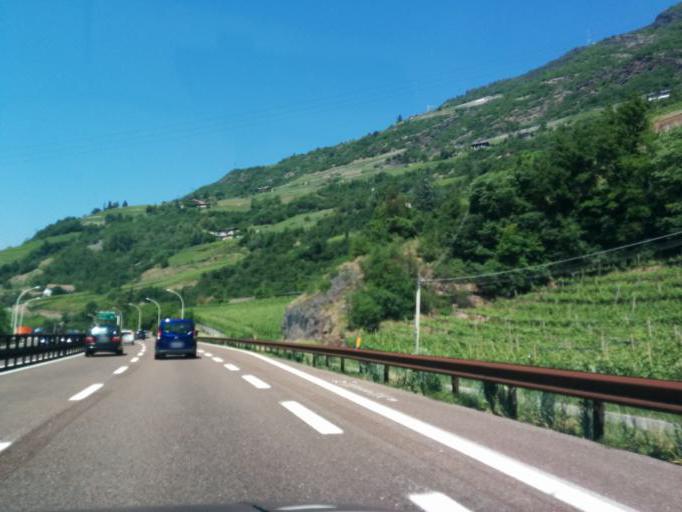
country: IT
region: Trentino-Alto Adige
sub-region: Bolzano
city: Cornedo All'Isarco
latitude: 46.4940
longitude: 11.4126
